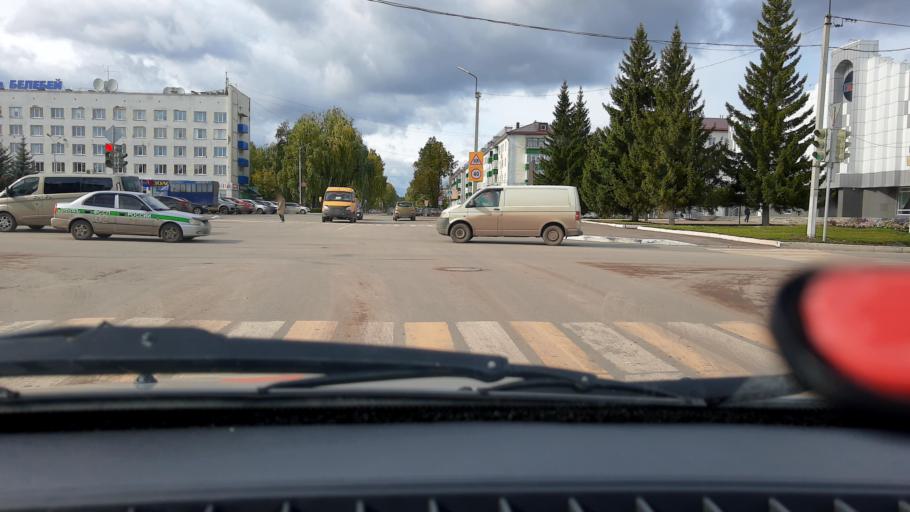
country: RU
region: Bashkortostan
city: Belebey
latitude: 54.1033
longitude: 54.1116
